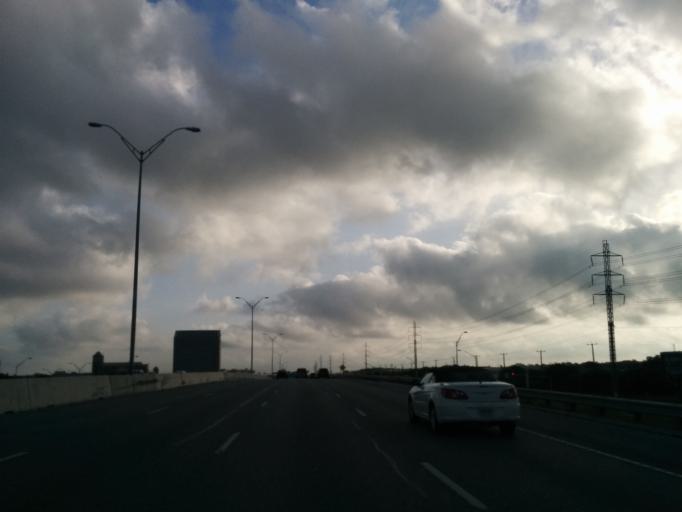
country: US
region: Texas
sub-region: Bexar County
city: Olmos Park
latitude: 29.4993
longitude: -98.4826
